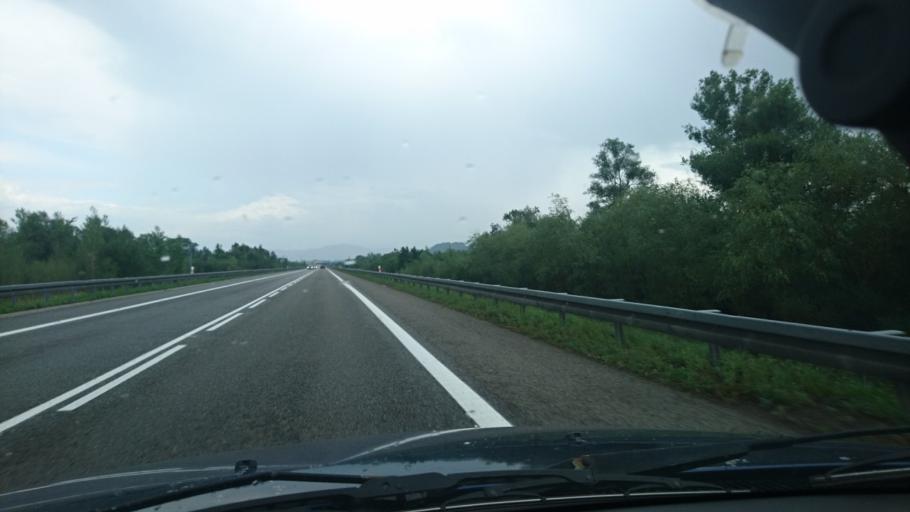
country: PL
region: Silesian Voivodeship
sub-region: Powiat zywiecki
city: Wieprz
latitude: 49.6390
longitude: 19.1667
